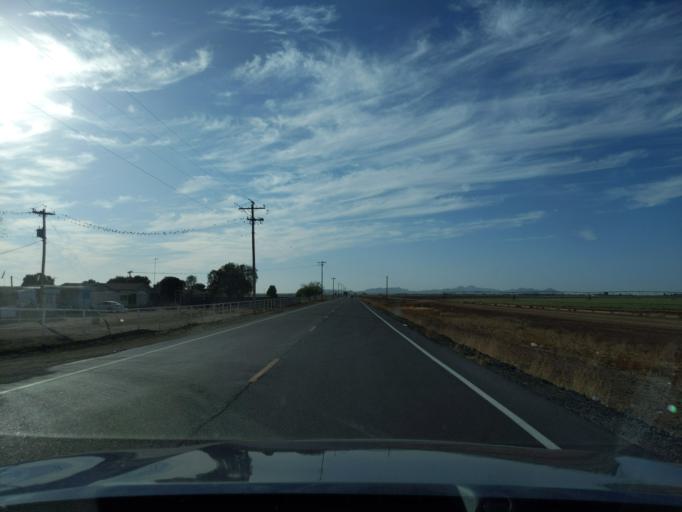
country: US
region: Arizona
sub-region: Pinal County
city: Florence
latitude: 33.1183
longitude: -111.4073
